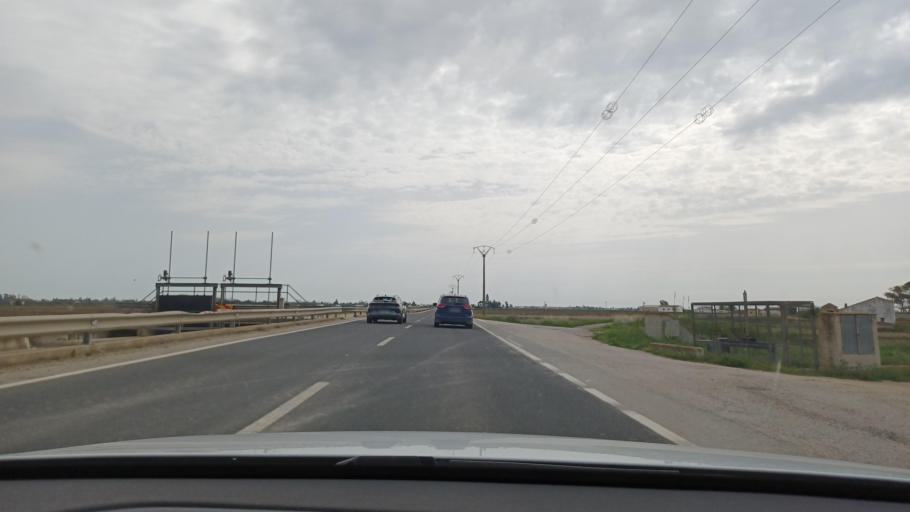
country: ES
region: Catalonia
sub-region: Provincia de Tarragona
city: Deltebre
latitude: 40.7103
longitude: 0.6600
